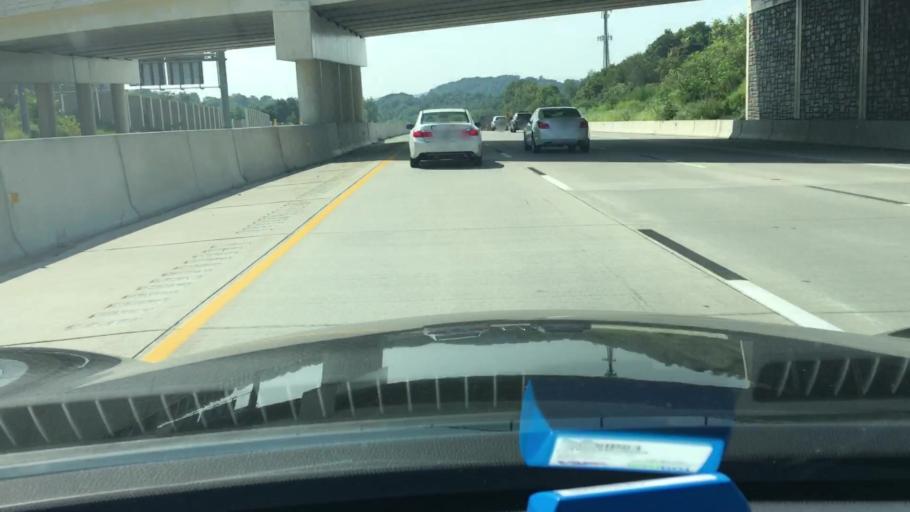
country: US
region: Pennsylvania
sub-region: Chester County
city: Malvern
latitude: 40.0522
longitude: -75.5337
